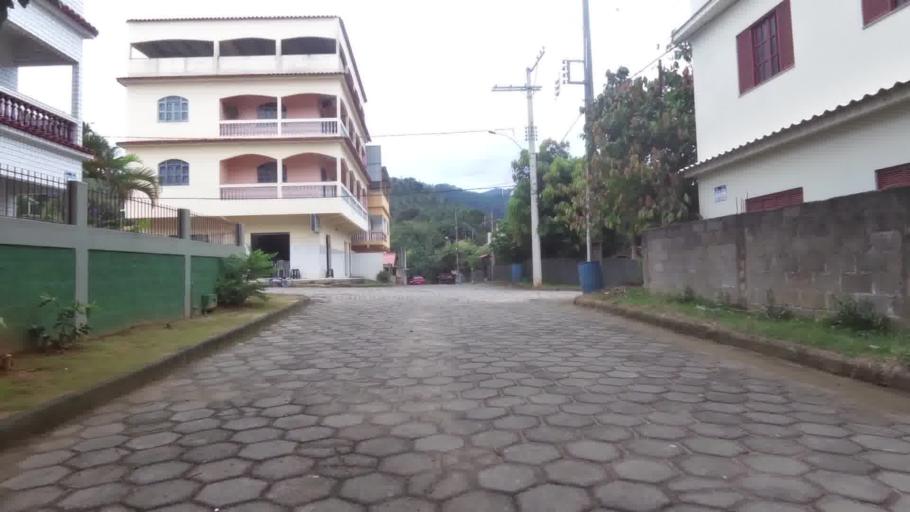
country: BR
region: Espirito Santo
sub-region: Iconha
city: Iconha
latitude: -20.7651
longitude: -40.8344
